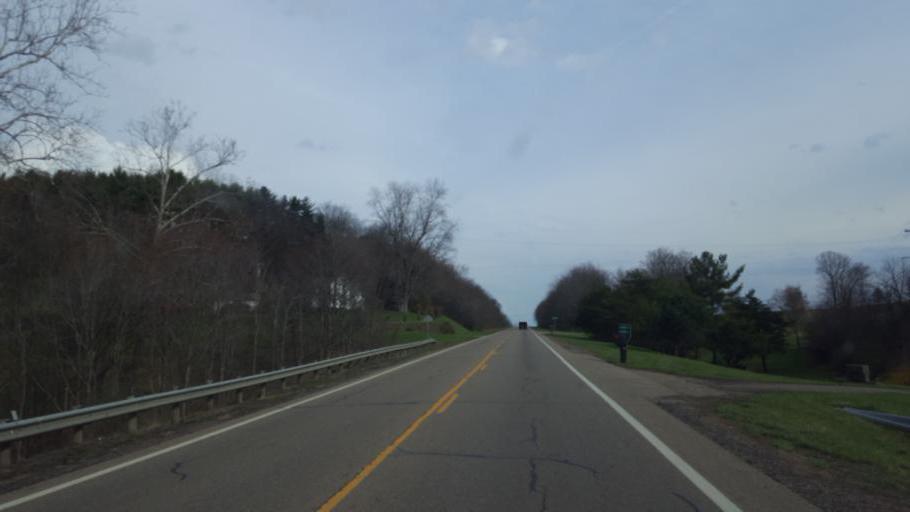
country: US
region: Ohio
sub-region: Coshocton County
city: Coshocton
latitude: 40.2366
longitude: -81.8579
